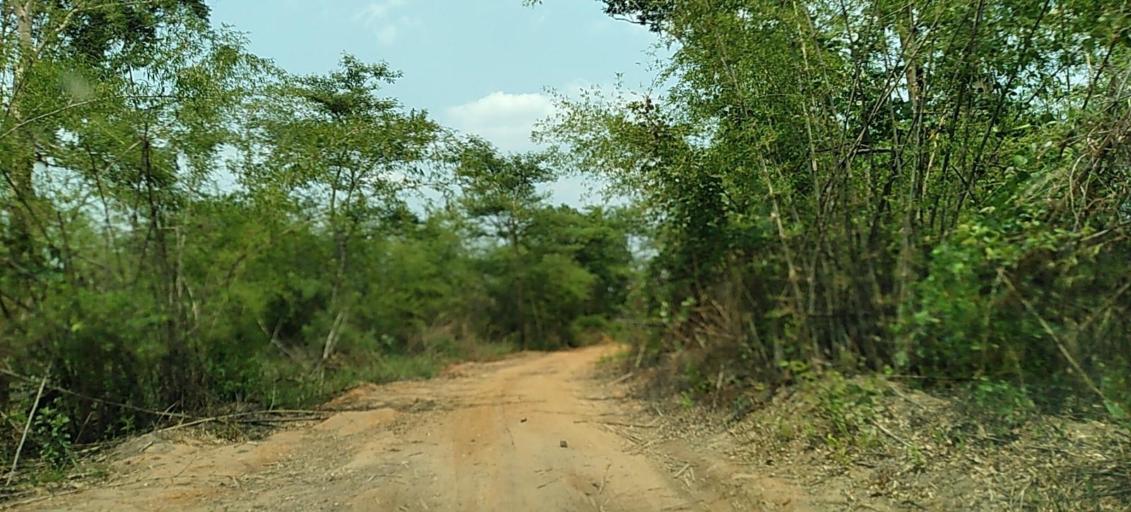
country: ZM
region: Copperbelt
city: Kalulushi
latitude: -12.7583
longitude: 28.0260
